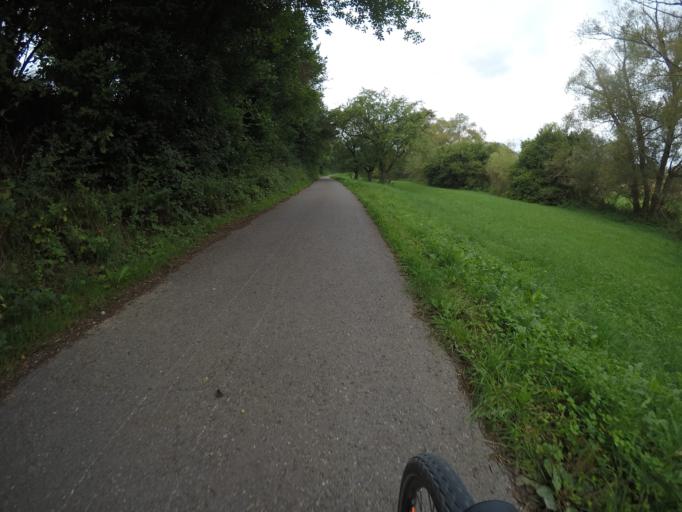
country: DE
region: Baden-Wuerttemberg
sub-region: Karlsruhe Region
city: Ostelsheim
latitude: 48.7441
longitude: 8.8405
